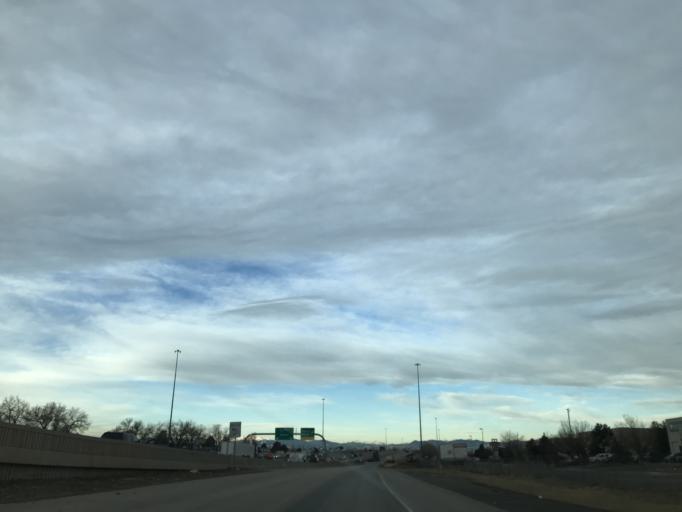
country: US
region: Colorado
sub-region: Adams County
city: Aurora
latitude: 39.7737
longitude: -104.8340
